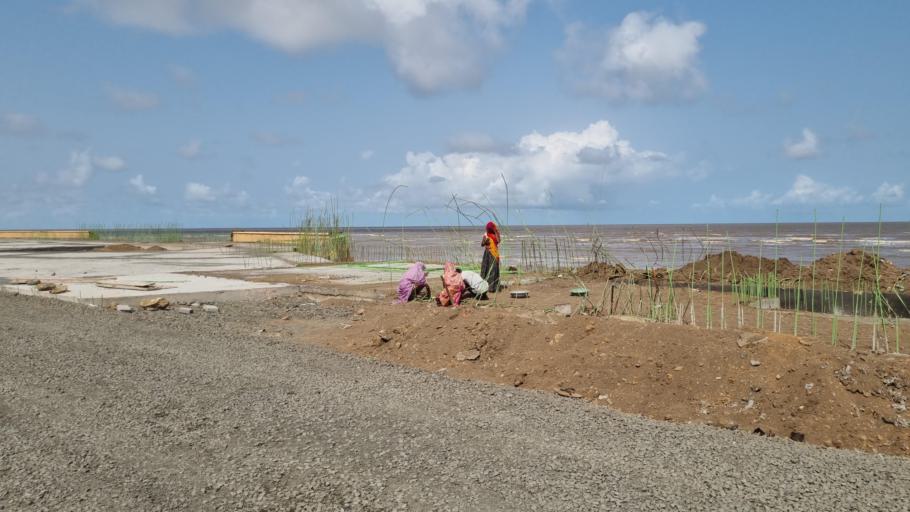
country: IN
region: Daman and Diu
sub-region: Daman District
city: Daman
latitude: 20.4452
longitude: 72.8325
